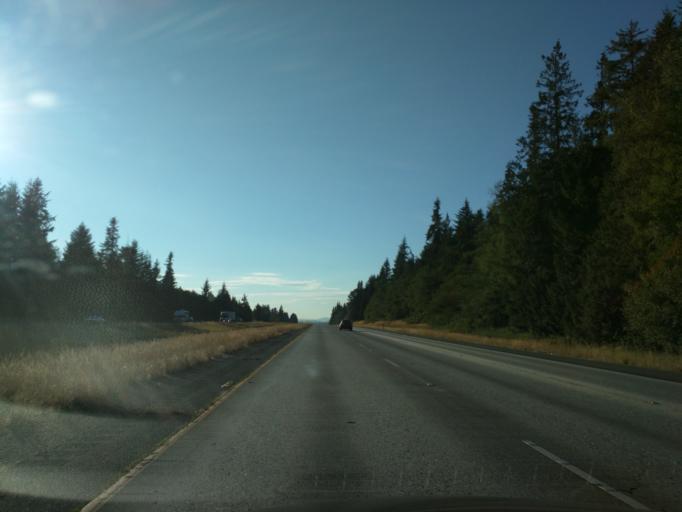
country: US
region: Washington
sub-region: Snohomish County
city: Stanwood
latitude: 48.2939
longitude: -122.2992
